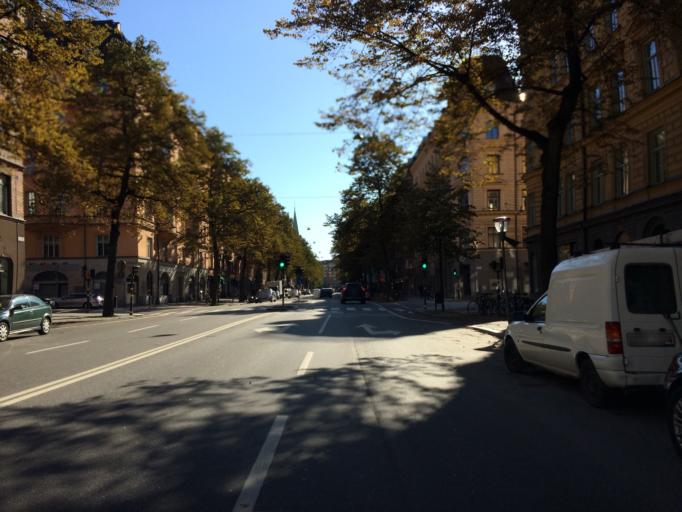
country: SE
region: Stockholm
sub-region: Stockholms Kommun
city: Stockholm
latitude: 59.3486
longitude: 18.0598
